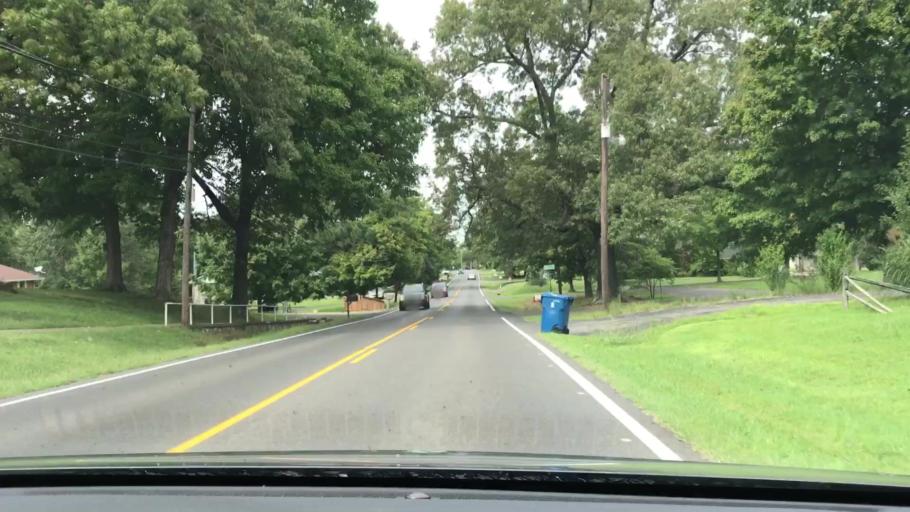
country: US
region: Kentucky
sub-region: Marshall County
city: Benton
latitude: 36.8435
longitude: -88.3498
